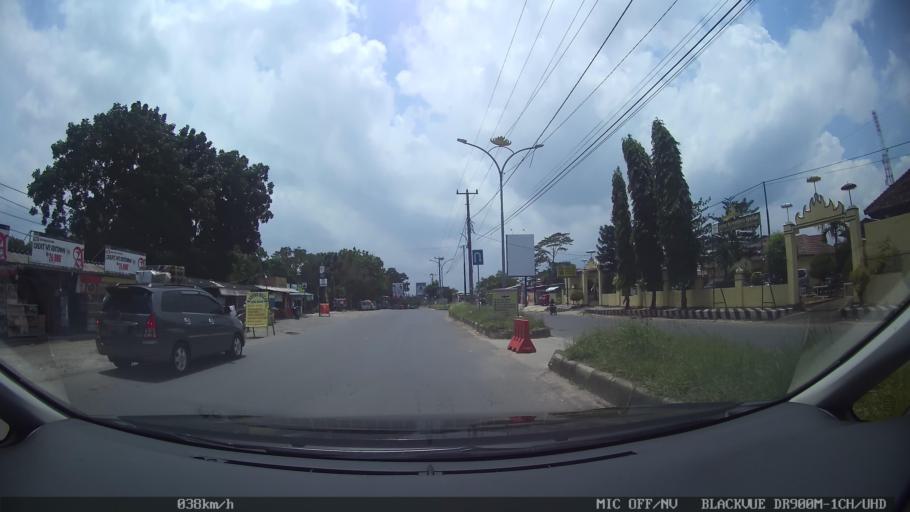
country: ID
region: Lampung
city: Kedaton
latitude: -5.3598
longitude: 105.3050
